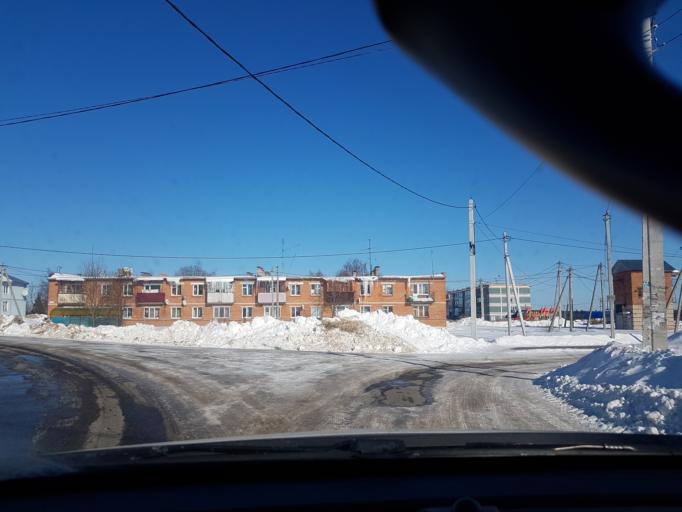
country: RU
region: Moskovskaya
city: Sychevo
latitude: 56.0142
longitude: 36.2240
